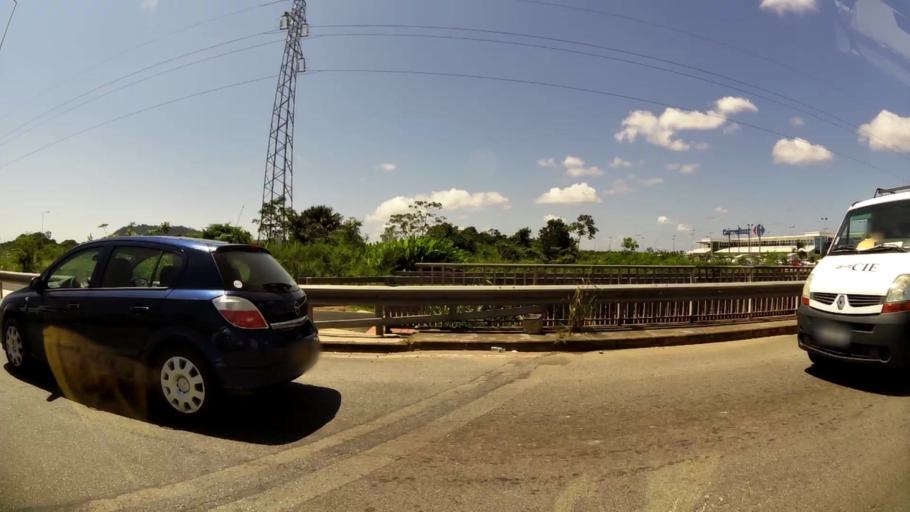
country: GF
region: Guyane
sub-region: Guyane
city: Cayenne
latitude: 4.8963
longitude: -52.3291
